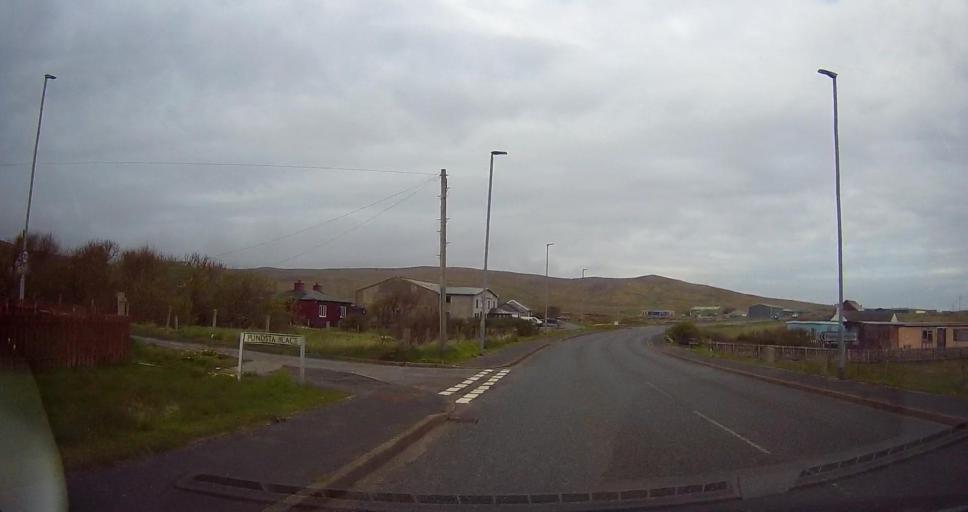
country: GB
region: Scotland
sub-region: Shetland Islands
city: Sandwick
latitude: 60.0542
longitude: -1.2256
